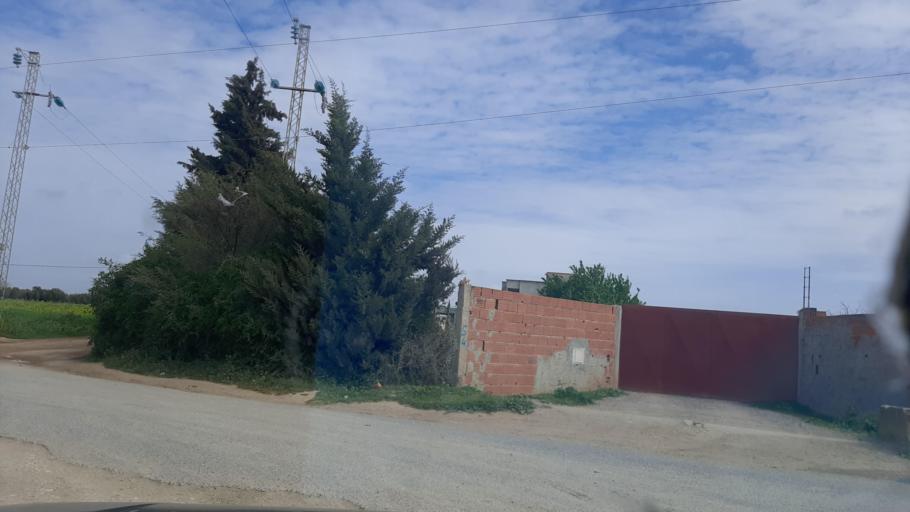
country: TN
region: Tunis
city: Oued Lill
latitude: 36.6983
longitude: 10.0028
